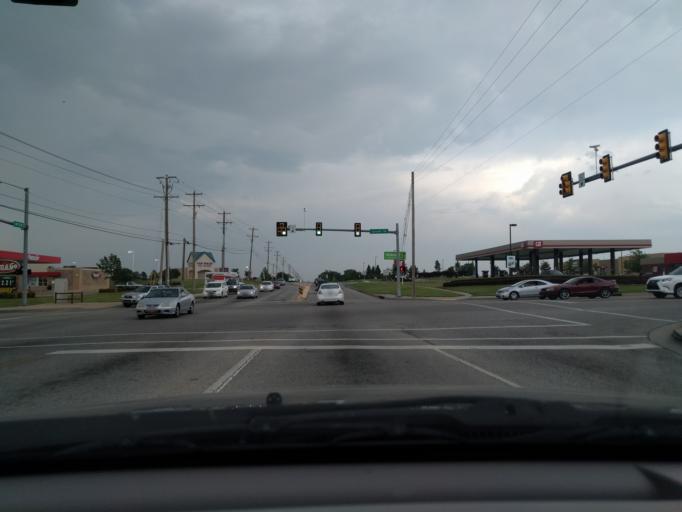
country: US
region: Oklahoma
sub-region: Tulsa County
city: Broken Arrow
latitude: 36.0464
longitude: -95.8514
